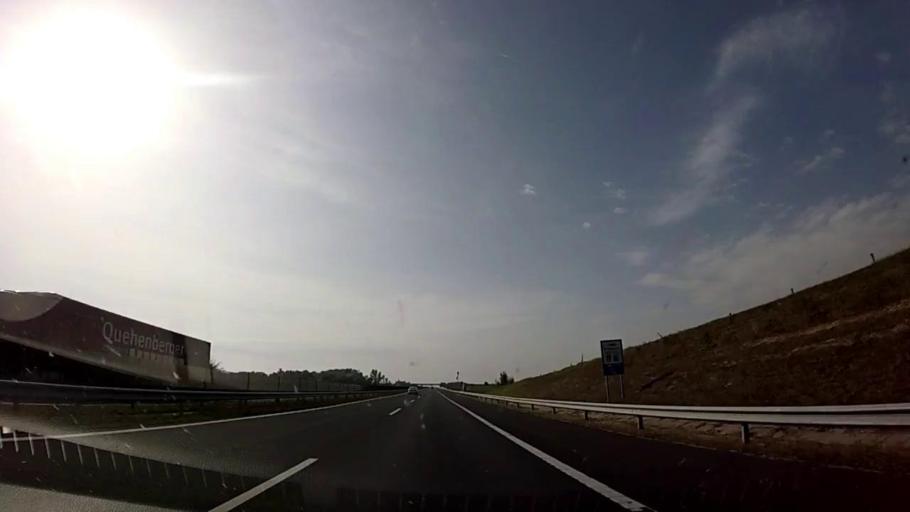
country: HU
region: Zala
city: Nagykanizsa
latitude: 46.4642
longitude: 16.8923
